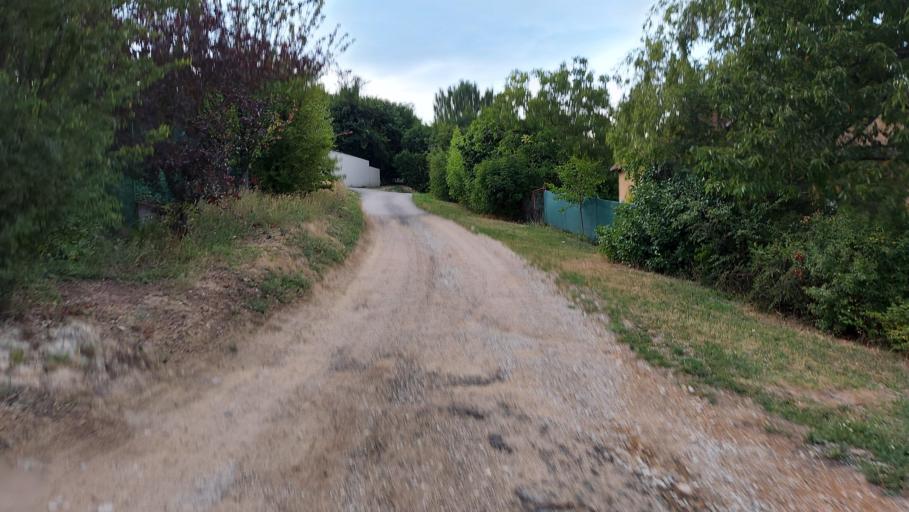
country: HU
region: Veszprem
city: Balatonalmadi
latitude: 47.0497
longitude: 18.0008
